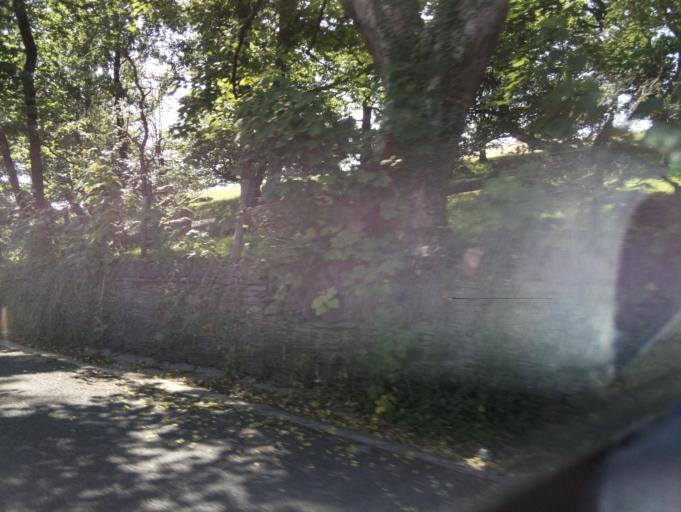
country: GB
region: Wales
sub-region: Caerphilly County Borough
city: Bargoed
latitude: 51.6996
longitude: -3.2309
